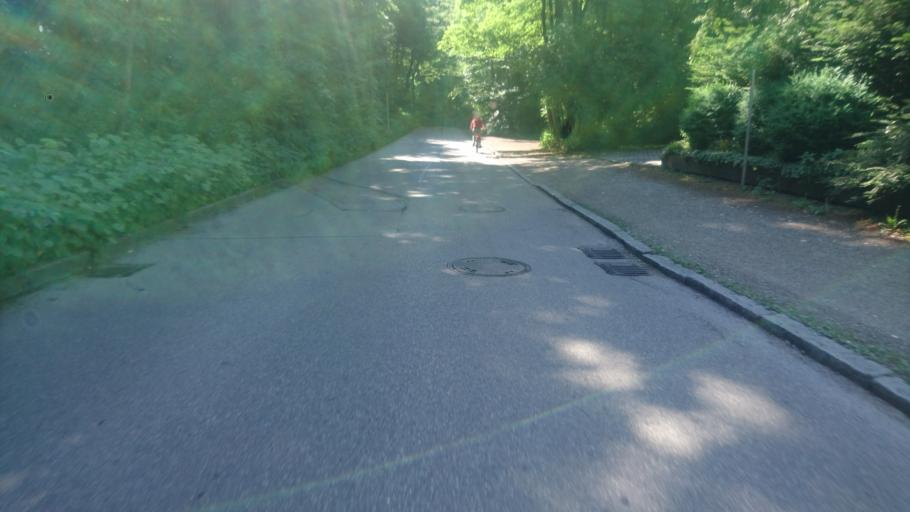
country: DE
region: Bavaria
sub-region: Upper Bavaria
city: Pullach im Isartal
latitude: 48.0774
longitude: 11.5343
